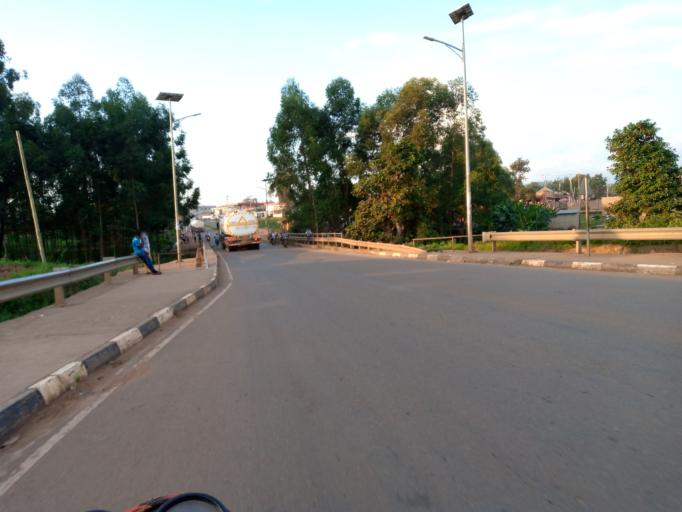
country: UG
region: Eastern Region
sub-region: Mbale District
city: Mbale
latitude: 1.0841
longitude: 34.1773
